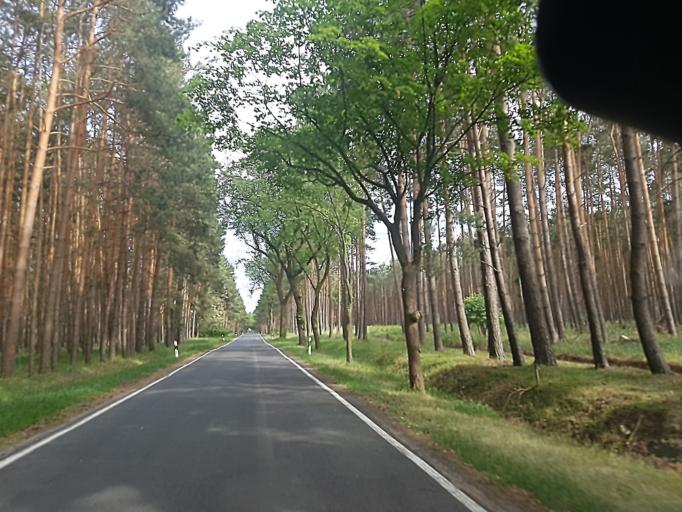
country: DE
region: Brandenburg
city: Belzig
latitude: 52.0710
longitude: 12.5541
